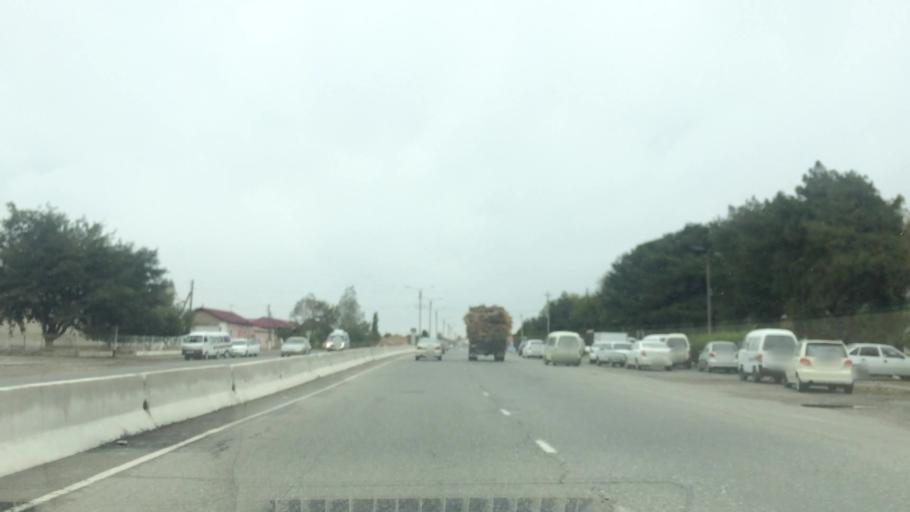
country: UZ
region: Samarqand
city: Bulung'ur
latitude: 39.7712
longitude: 67.2747
